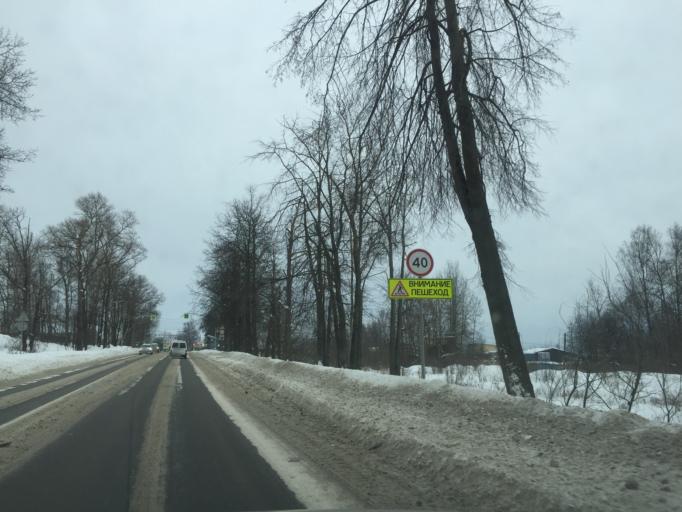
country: RU
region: Leningrad
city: Yanino Vtoroye
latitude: 59.9303
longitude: 30.6173
